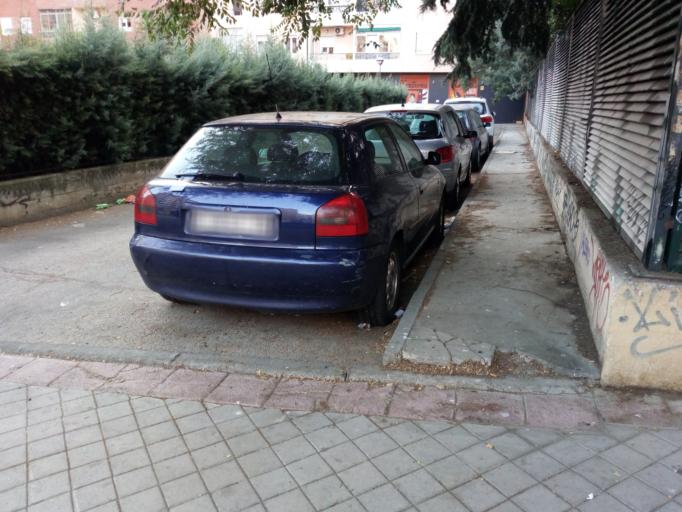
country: ES
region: Madrid
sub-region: Provincia de Madrid
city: Retiro
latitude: 40.4076
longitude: -3.6690
